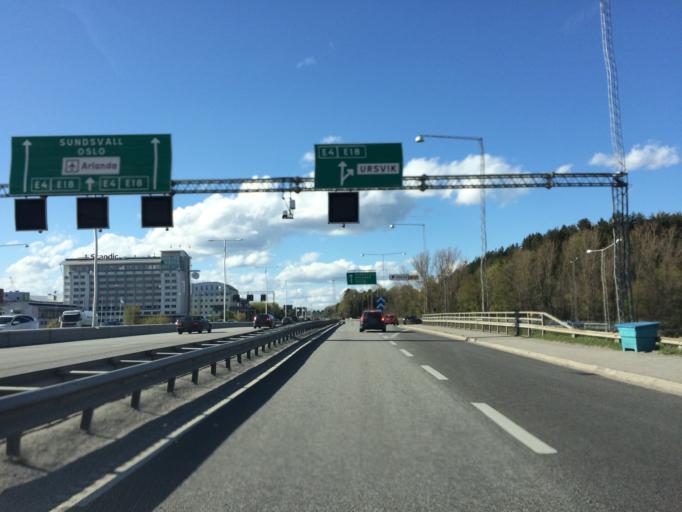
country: SE
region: Stockholm
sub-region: Norrtalje Kommun
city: Bergshamra
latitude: 59.3780
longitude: 18.0135
